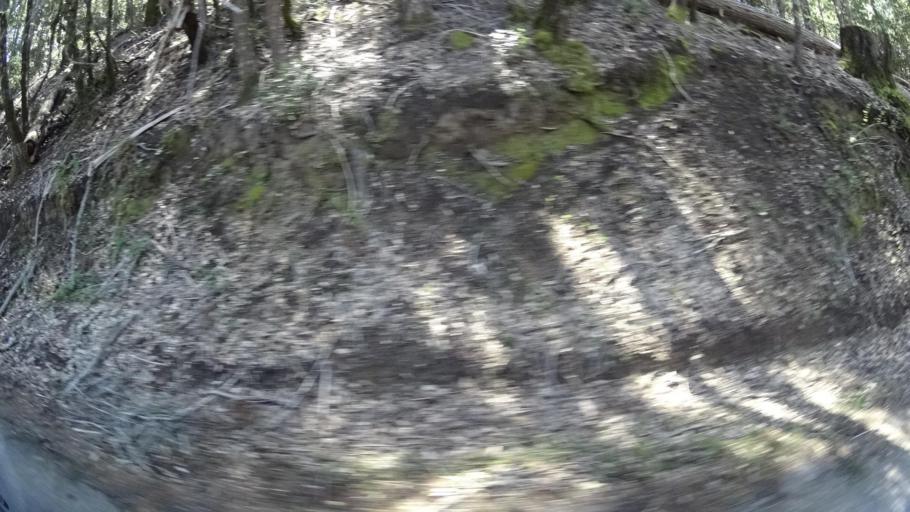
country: US
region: California
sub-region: Humboldt County
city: Rio Dell
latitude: 40.3037
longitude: -124.0621
